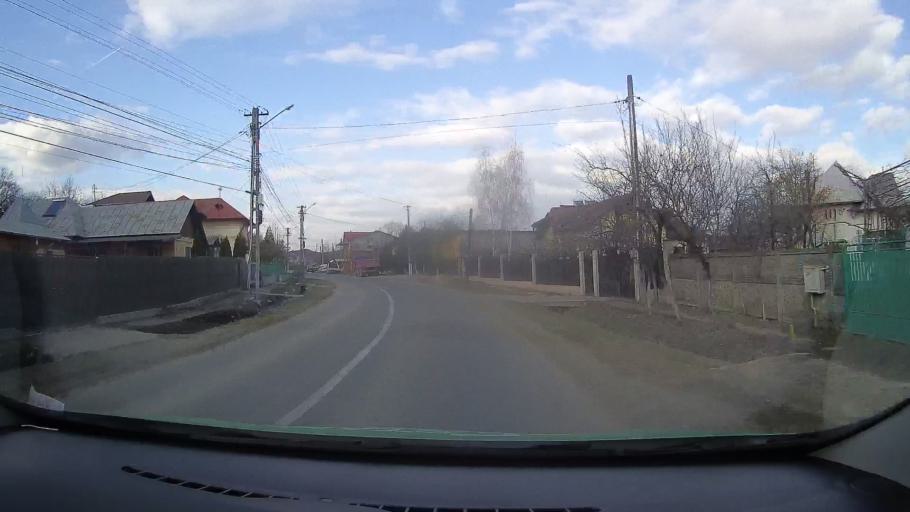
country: RO
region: Dambovita
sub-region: Comuna Gura Ocnitei
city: Gura Ocnitei
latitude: 44.9338
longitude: 25.5619
